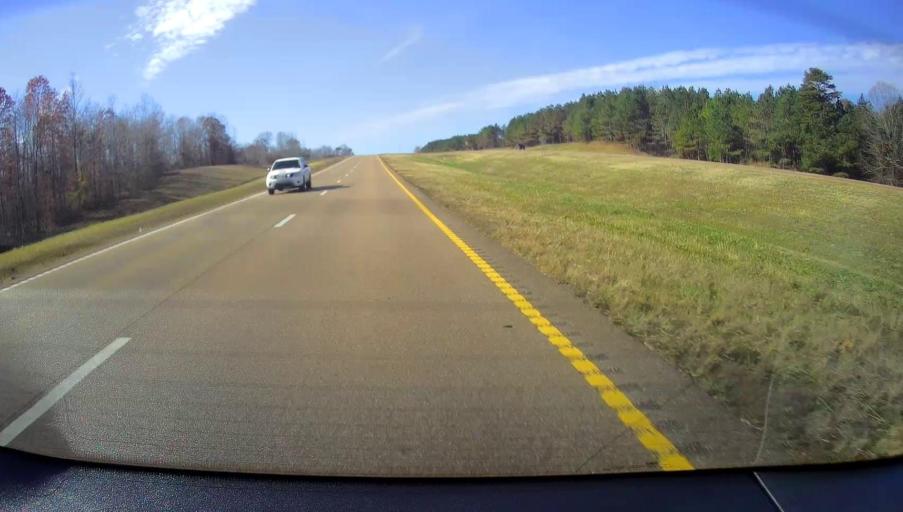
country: US
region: Mississippi
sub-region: Benton County
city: Ashland
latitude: 34.9497
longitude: -89.0897
